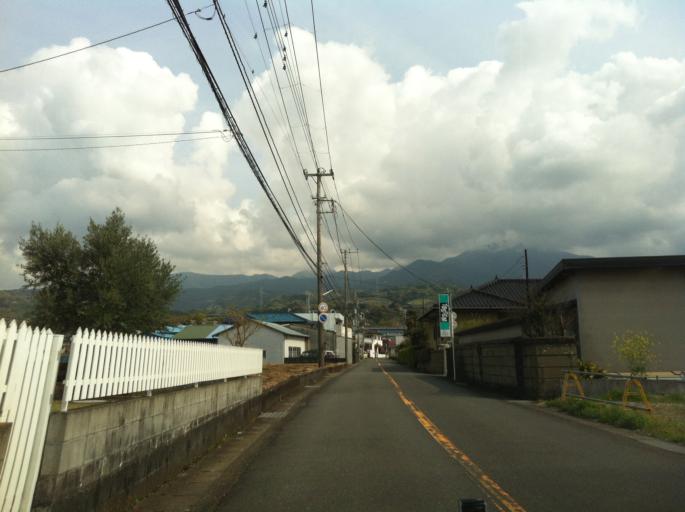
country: JP
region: Shizuoka
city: Fuji
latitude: 35.1461
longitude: 138.7777
